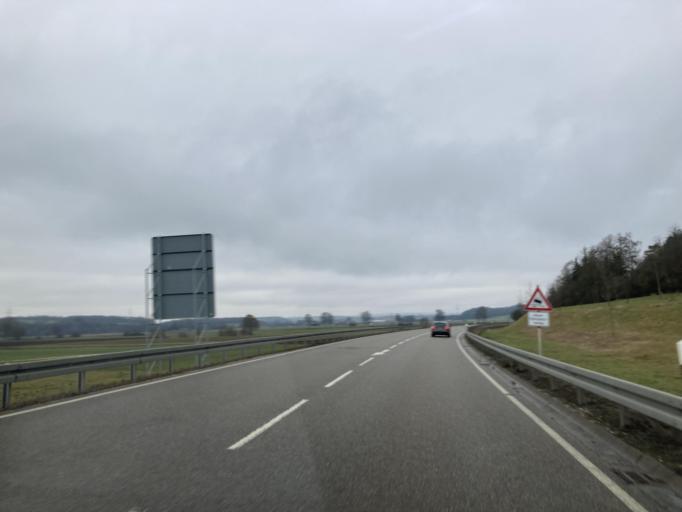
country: DE
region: Baden-Wuerttemberg
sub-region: Regierungsbezirk Stuttgart
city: Sontheim an der Brenz
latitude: 48.5735
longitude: 10.2914
